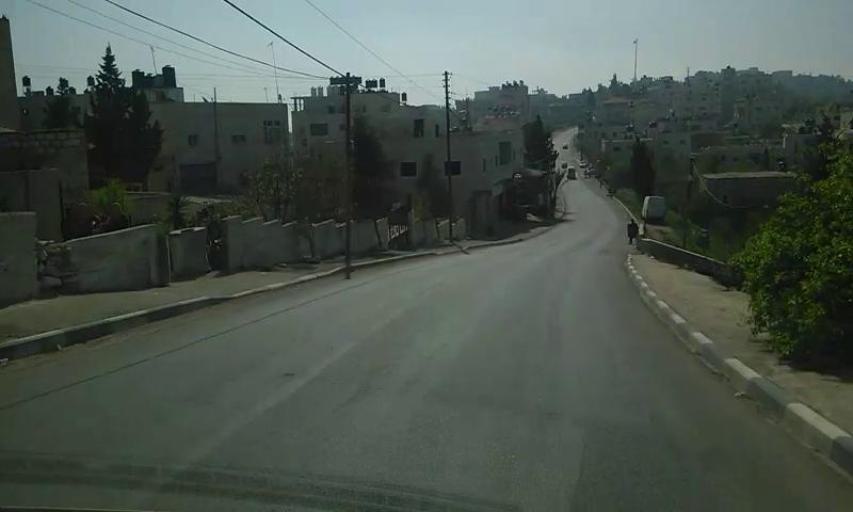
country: PS
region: West Bank
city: Dayr Jarir
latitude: 31.9617
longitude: 35.2956
